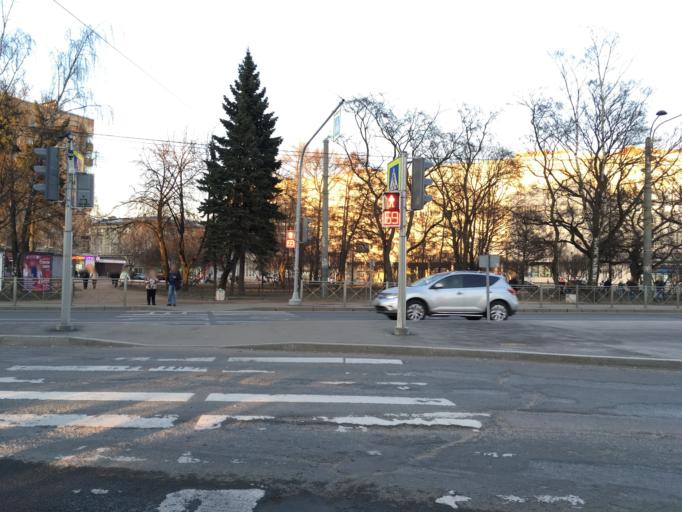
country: RU
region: St.-Petersburg
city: Kushelevka
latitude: 59.9995
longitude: 30.3632
